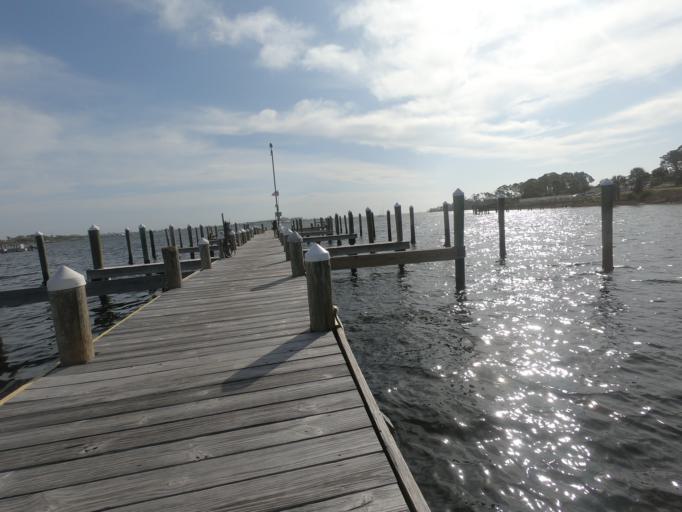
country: US
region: Florida
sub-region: Bay County
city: Lower Grand Lagoon
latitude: 30.1430
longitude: -85.7460
